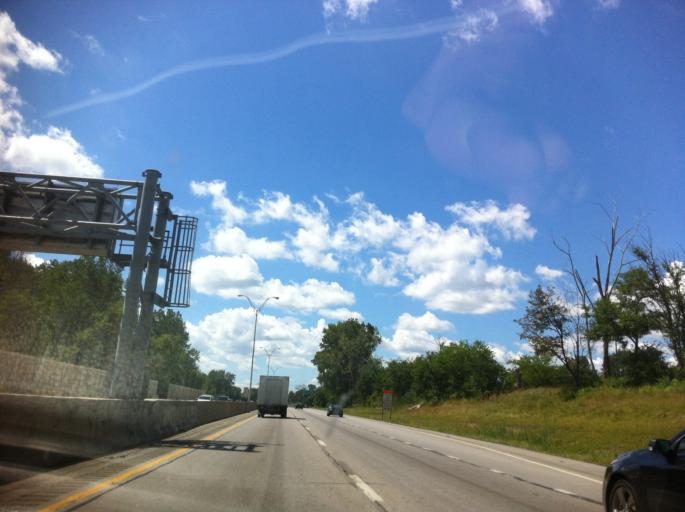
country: US
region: Ohio
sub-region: Lucas County
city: Ottawa Hills
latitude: 41.6883
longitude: -83.6359
